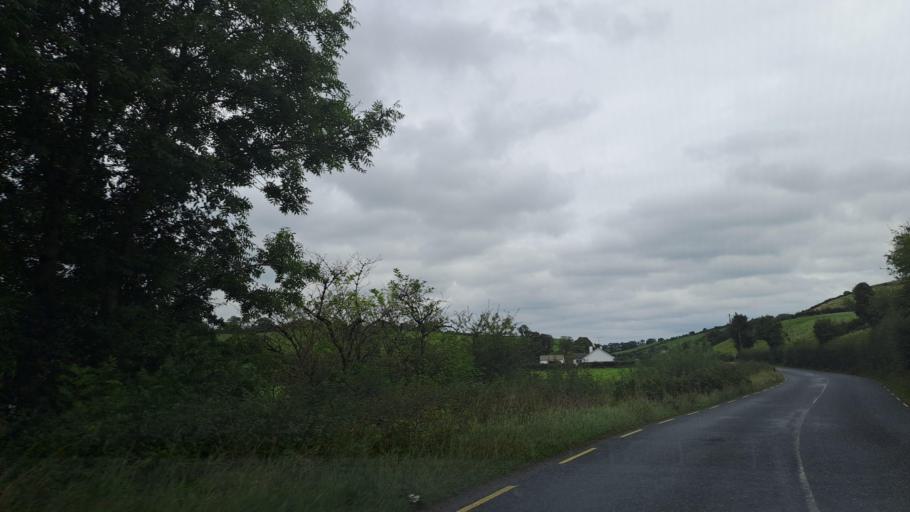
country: IE
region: Ulster
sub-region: An Cabhan
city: Bailieborough
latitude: 53.9615
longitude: -6.9243
